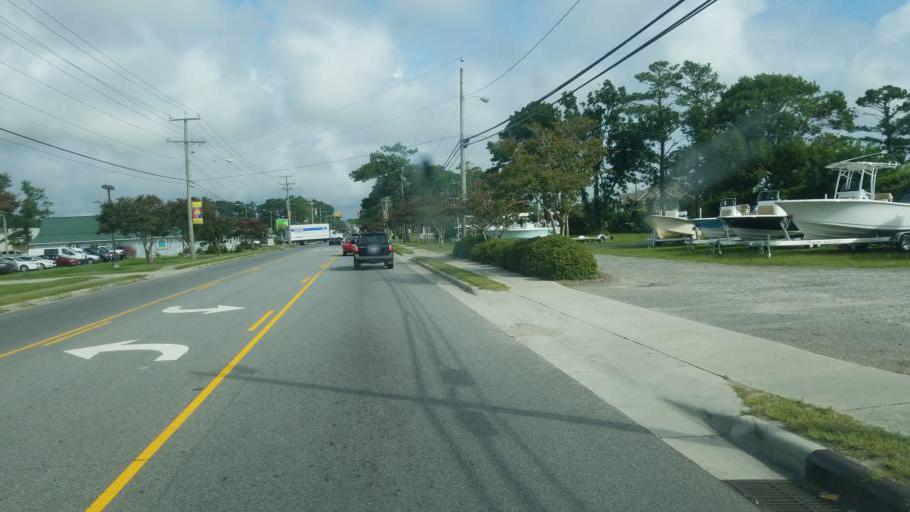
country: US
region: North Carolina
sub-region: Dare County
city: Manteo
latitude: 35.9010
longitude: -75.6706
